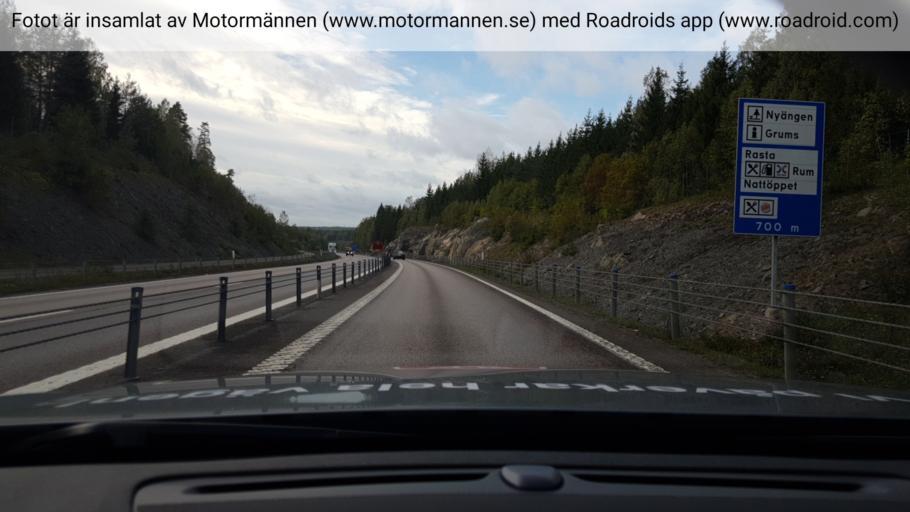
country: SE
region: Vaermland
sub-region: Karlstads Kommun
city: Valberg
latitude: 59.3705
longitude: 13.1581
